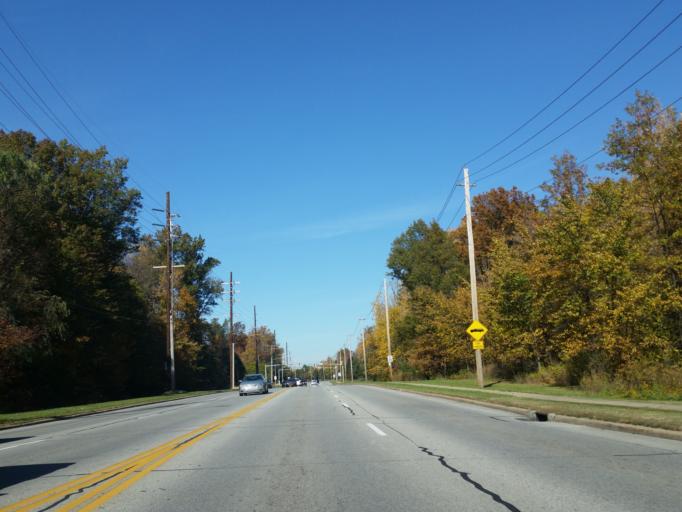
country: US
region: Ohio
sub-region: Cuyahoga County
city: Westlake
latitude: 41.4402
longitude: -81.9474
